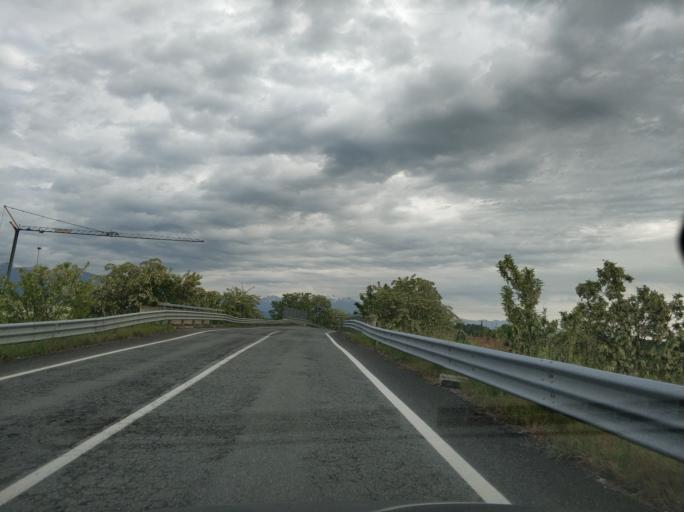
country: IT
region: Piedmont
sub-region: Provincia di Torino
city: San Maurizio
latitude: 45.2209
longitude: 7.6193
